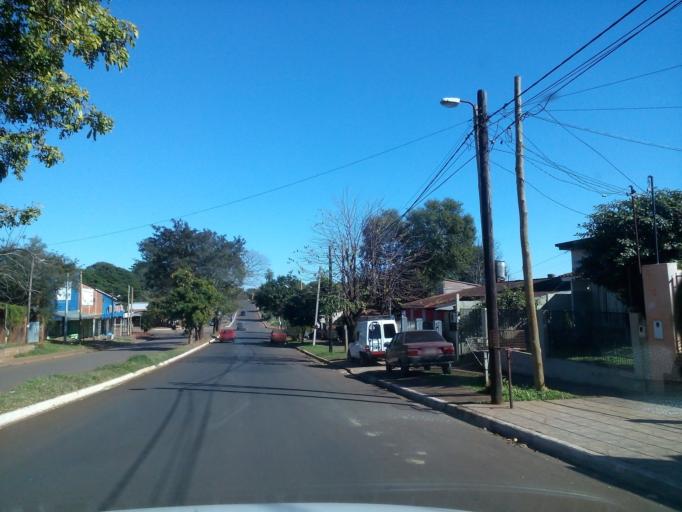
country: AR
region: Misiones
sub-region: Departamento de Capital
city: Posadas
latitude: -27.3774
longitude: -55.9318
